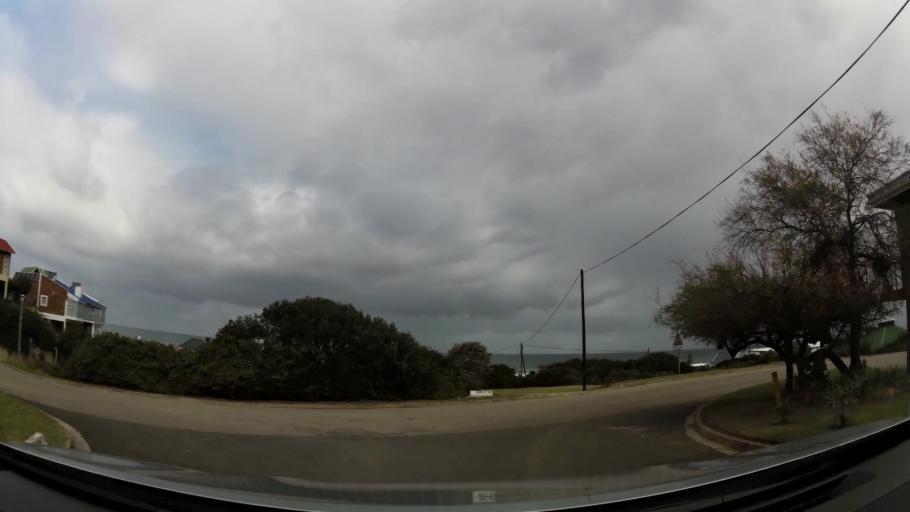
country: ZA
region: Western Cape
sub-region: Eden District Municipality
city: George
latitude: -34.0486
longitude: 22.3150
